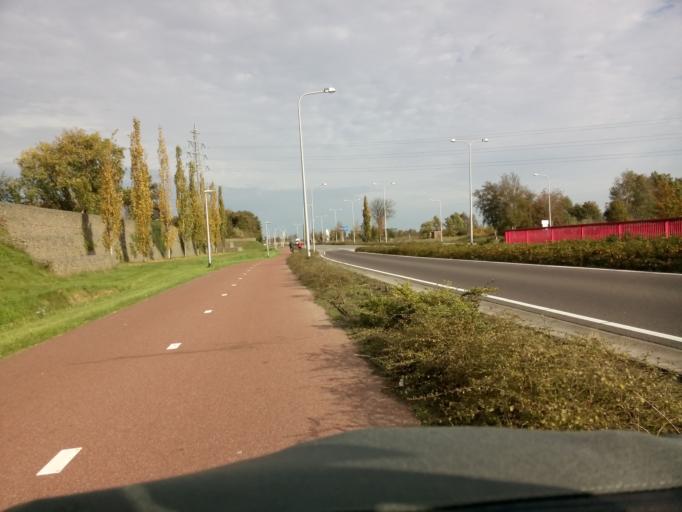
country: NL
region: Drenthe
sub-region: Gemeente Assen
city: Assen
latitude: 53.0188
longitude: 6.5710
